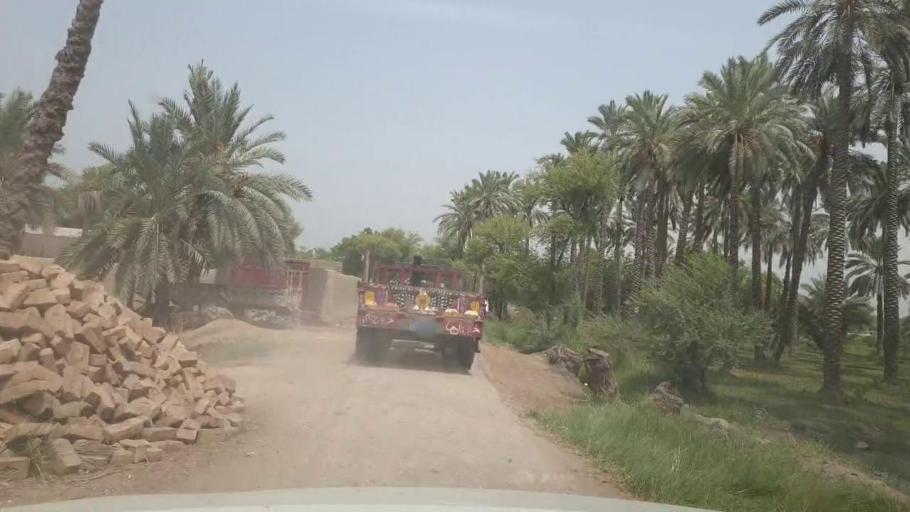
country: PK
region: Sindh
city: Kot Diji
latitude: 27.3507
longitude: 68.7030
